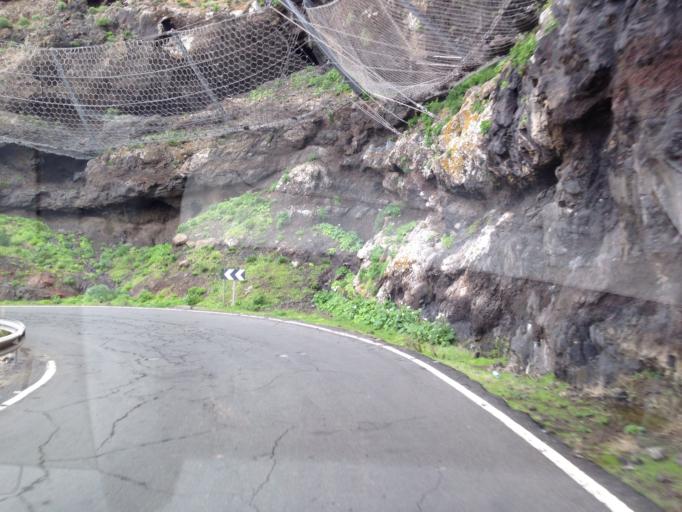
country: ES
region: Canary Islands
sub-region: Provincia de Las Palmas
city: San Nicolas
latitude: 28.0313
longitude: -15.7636
